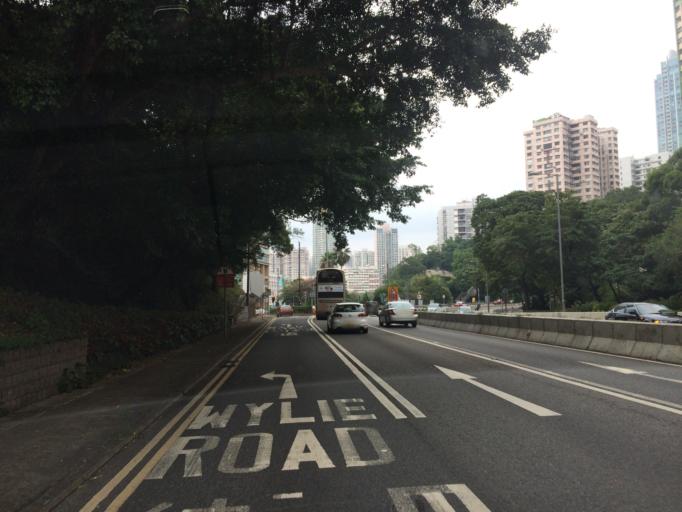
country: HK
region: Kowloon City
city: Kowloon
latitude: 22.3115
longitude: 114.1772
